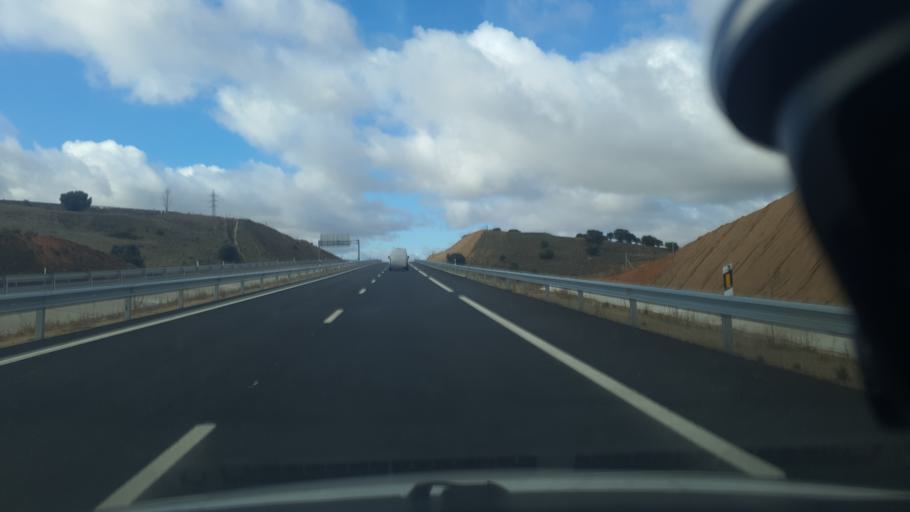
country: ES
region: Castille and Leon
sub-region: Provincia de Segovia
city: Segovia
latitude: 40.9195
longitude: -4.1268
